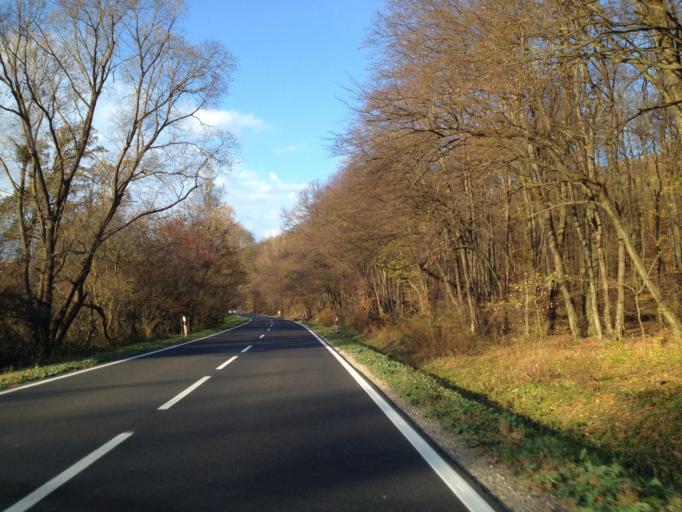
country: HU
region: Gyor-Moson-Sopron
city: Bakonyszentlaszlo
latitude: 47.3889
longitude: 17.8652
